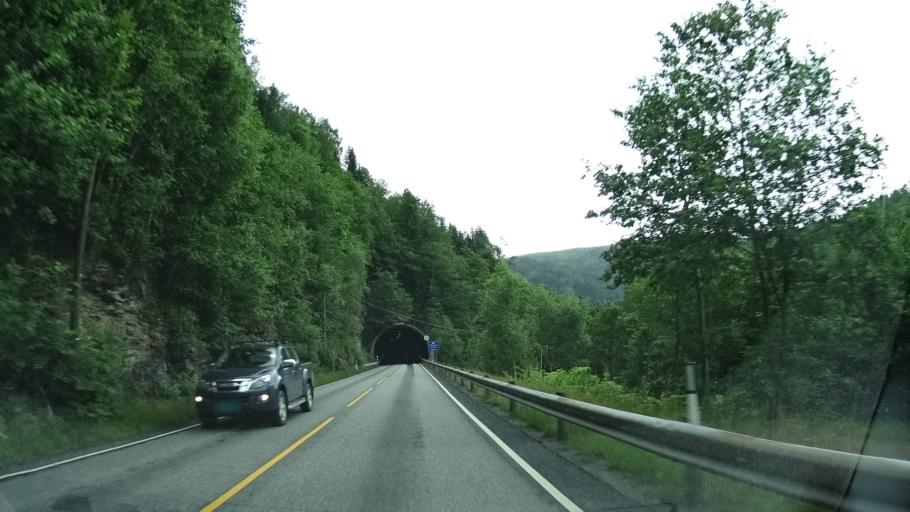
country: NO
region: Hordaland
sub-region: Granvin
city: Granvin
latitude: 60.5391
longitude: 6.7263
